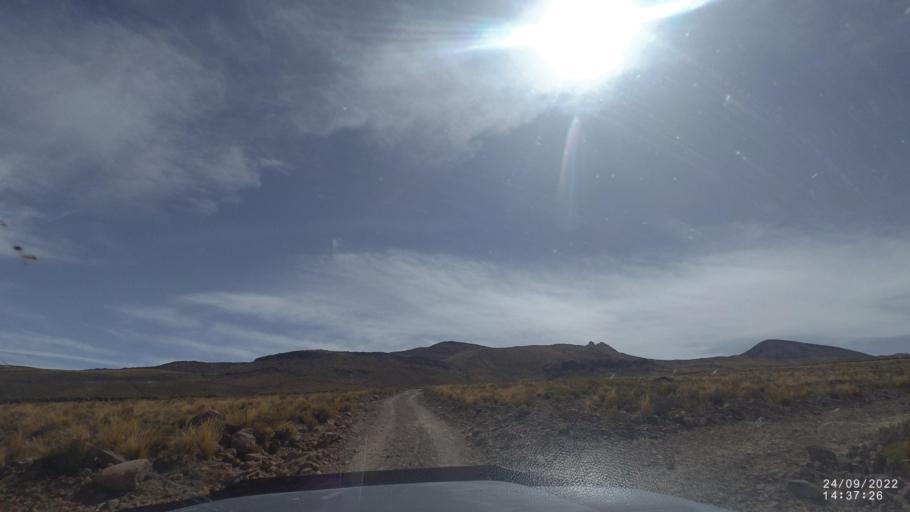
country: BO
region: Potosi
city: Colchani
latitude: -19.8543
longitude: -67.5825
